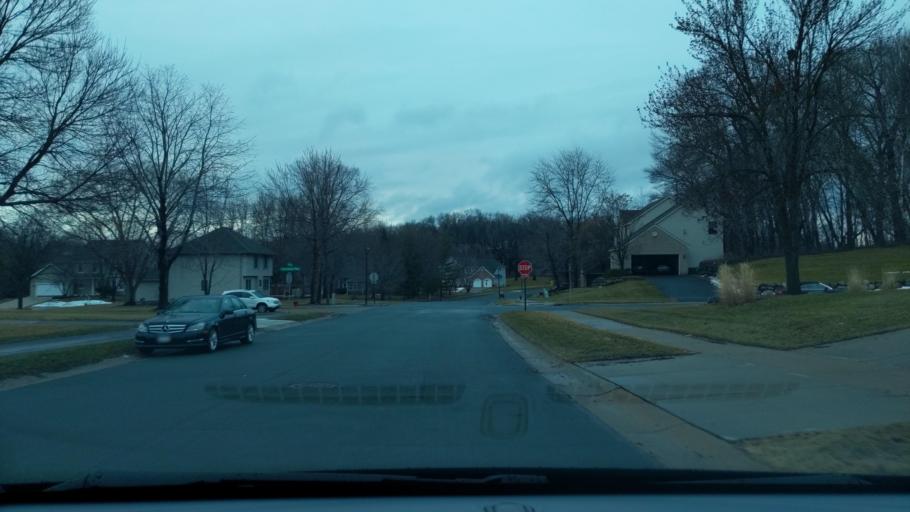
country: US
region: Minnesota
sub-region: Hennepin County
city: Eden Prairie
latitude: 44.8458
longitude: -93.4911
